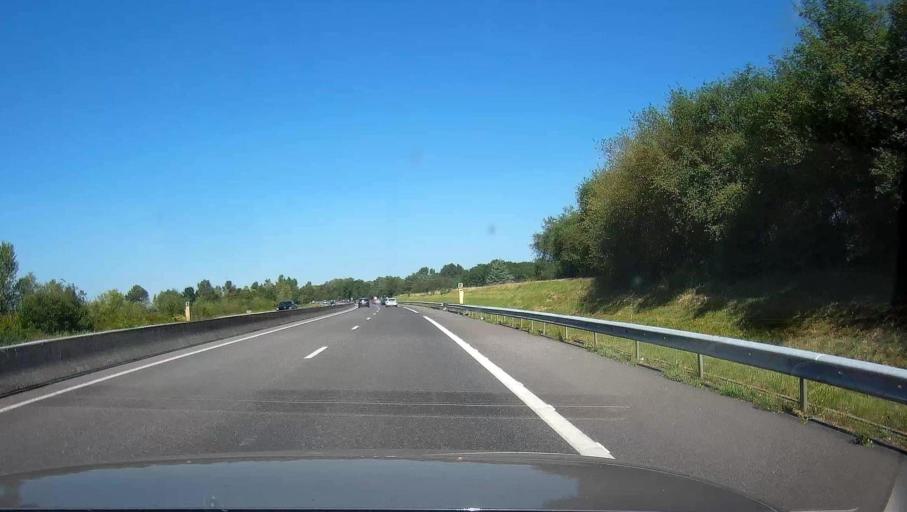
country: FR
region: Champagne-Ardenne
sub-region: Departement de la Marne
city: Fagnieres
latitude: 49.0061
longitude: 4.2991
